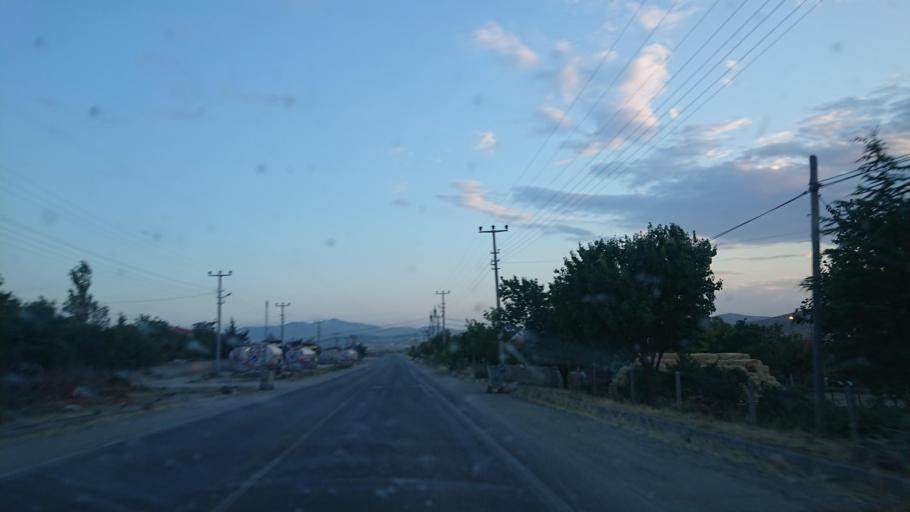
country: TR
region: Aksaray
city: Balci
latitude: 38.7882
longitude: 34.1214
